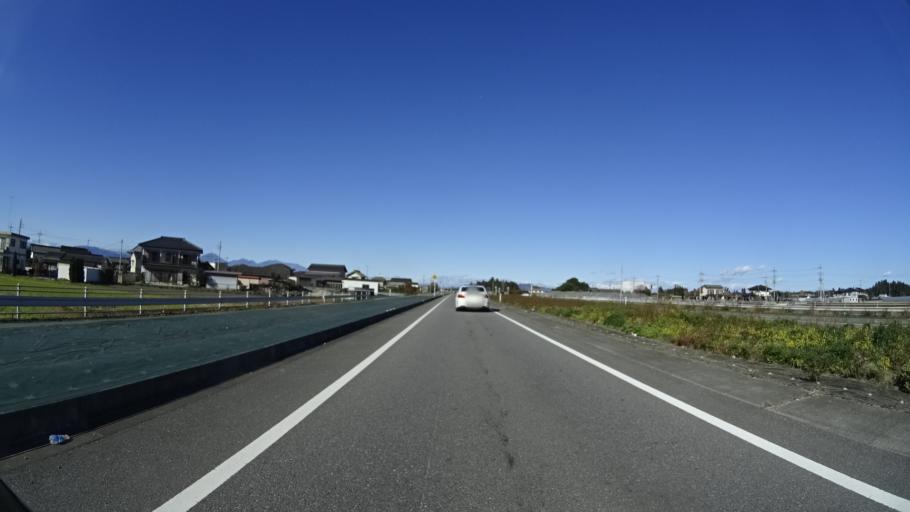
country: JP
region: Tochigi
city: Kanuma
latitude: 36.4802
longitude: 139.7539
